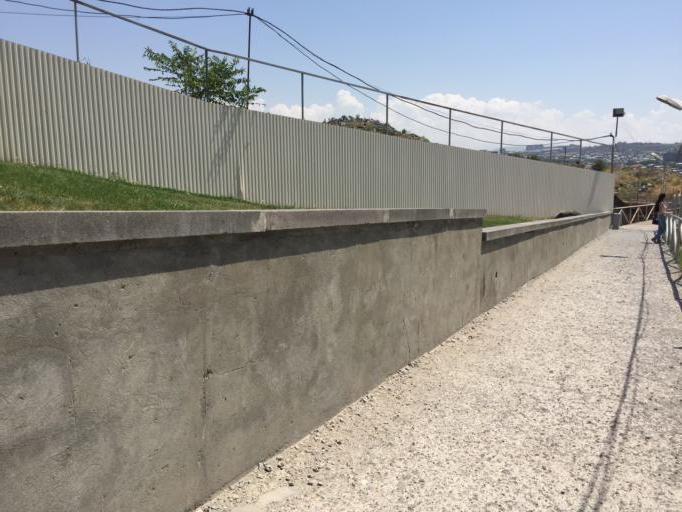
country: AM
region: Yerevan
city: Yerevan
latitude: 40.1931
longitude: 44.5147
